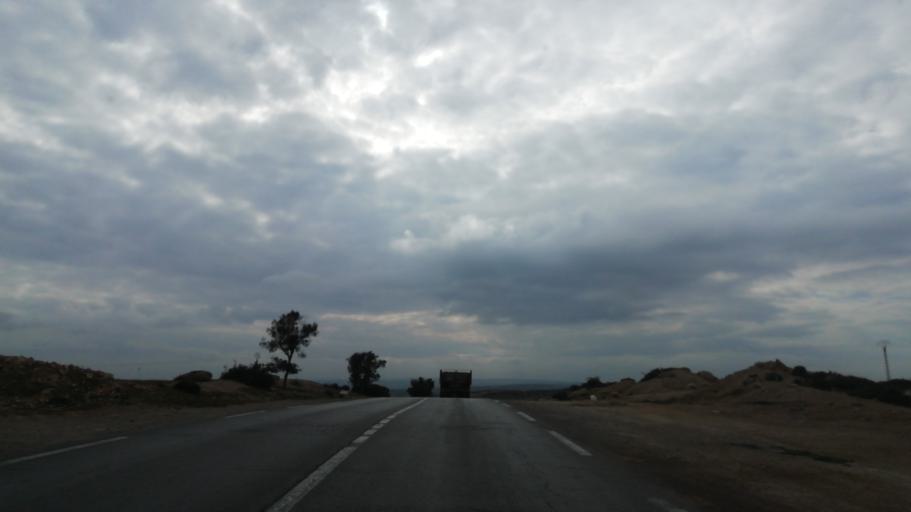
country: DZ
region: Oran
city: Ain el Bya
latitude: 35.7296
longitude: -0.3547
